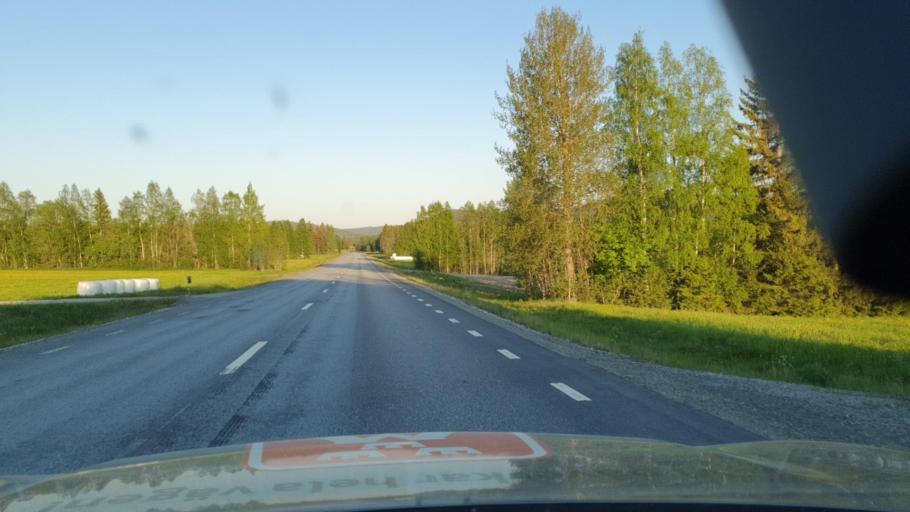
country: SE
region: Vaesternorrland
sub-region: Solleftea Kommun
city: Solleftea
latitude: 63.3286
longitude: 17.1536
